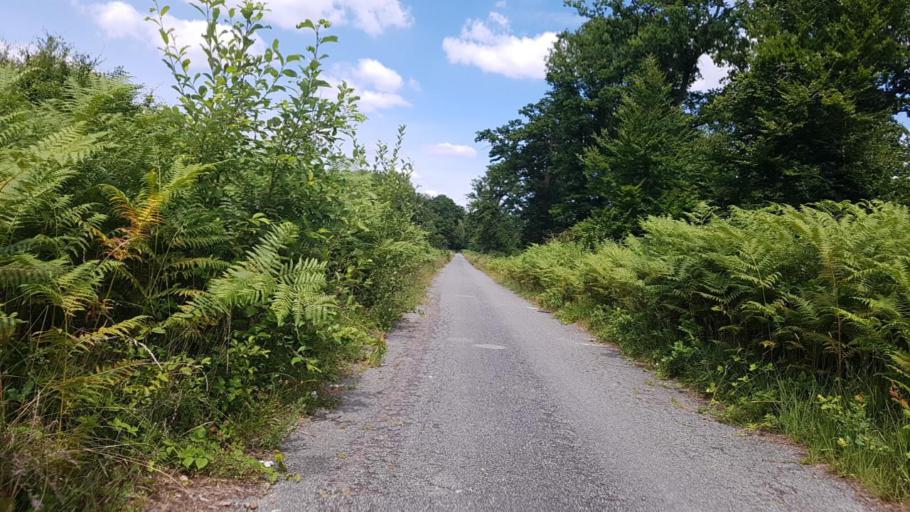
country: FR
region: Picardie
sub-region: Departement de l'Oise
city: Le Plessis-Brion
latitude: 49.4600
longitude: 2.9087
